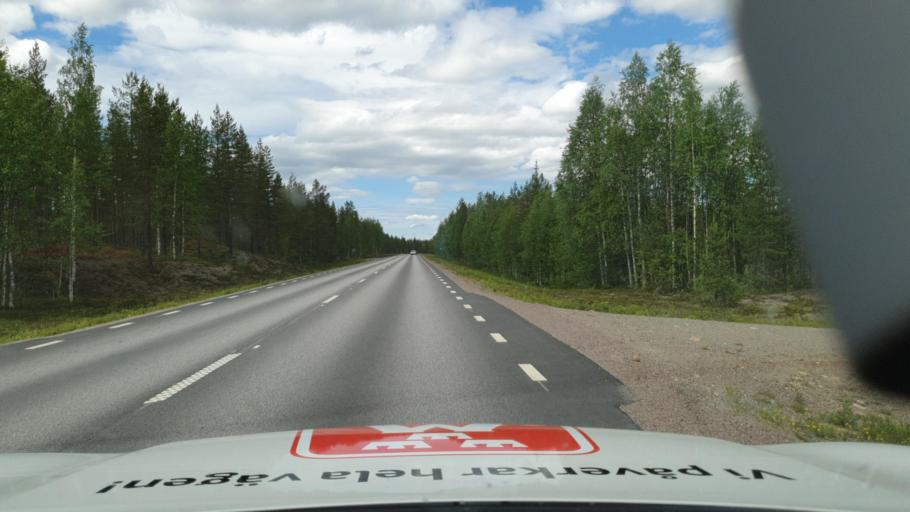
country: SE
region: Vaesterbotten
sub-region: Skelleftea Kommun
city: Langsele
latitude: 65.1387
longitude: 19.9064
